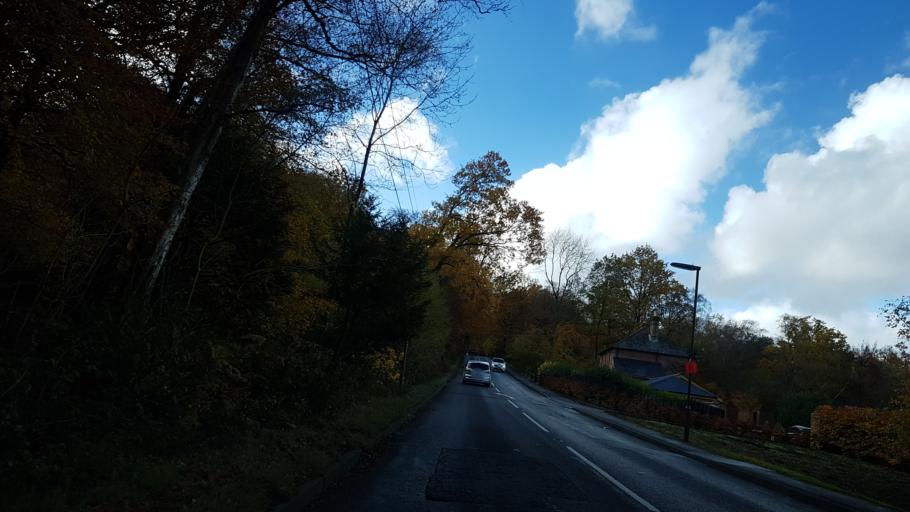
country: GB
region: England
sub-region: Surrey
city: Haslemere
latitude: 51.1003
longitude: -0.6966
